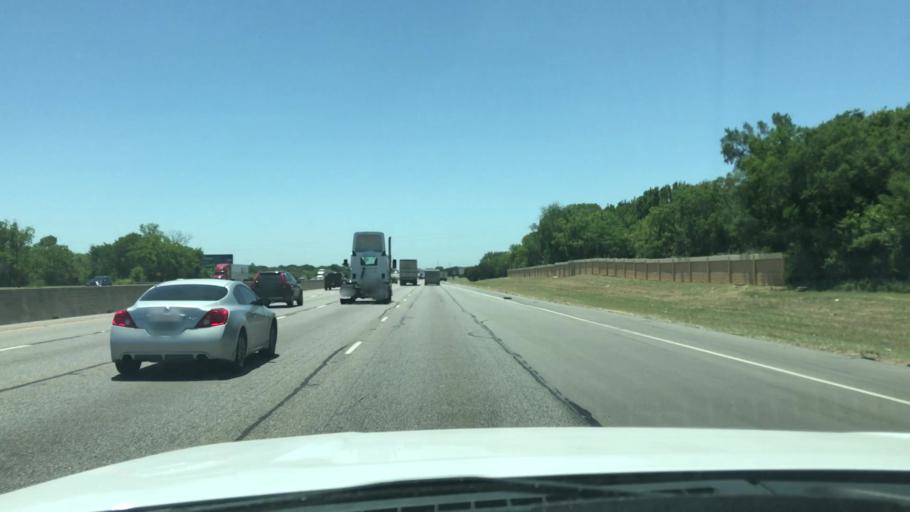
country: US
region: Texas
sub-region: Dallas County
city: Balch Springs
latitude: 32.6856
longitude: -96.6456
